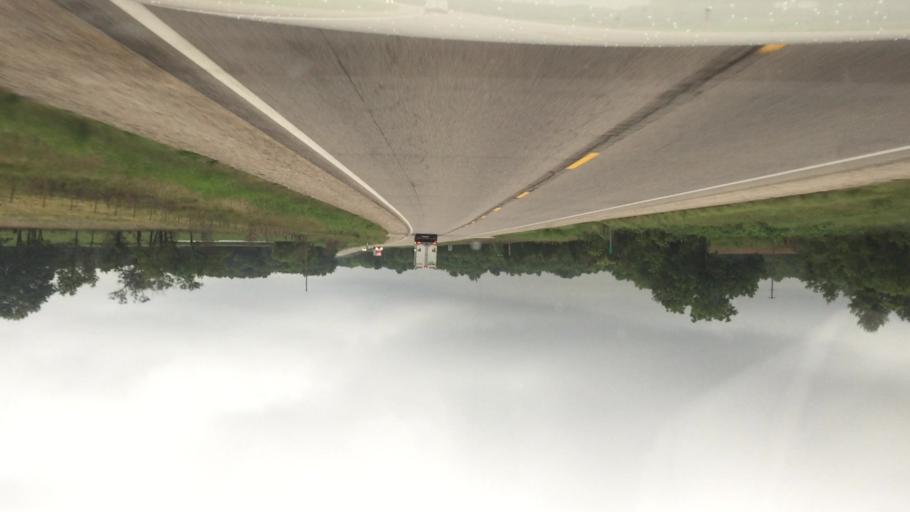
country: US
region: Kansas
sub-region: Montgomery County
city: Coffeyville
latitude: 37.1376
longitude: -95.5770
